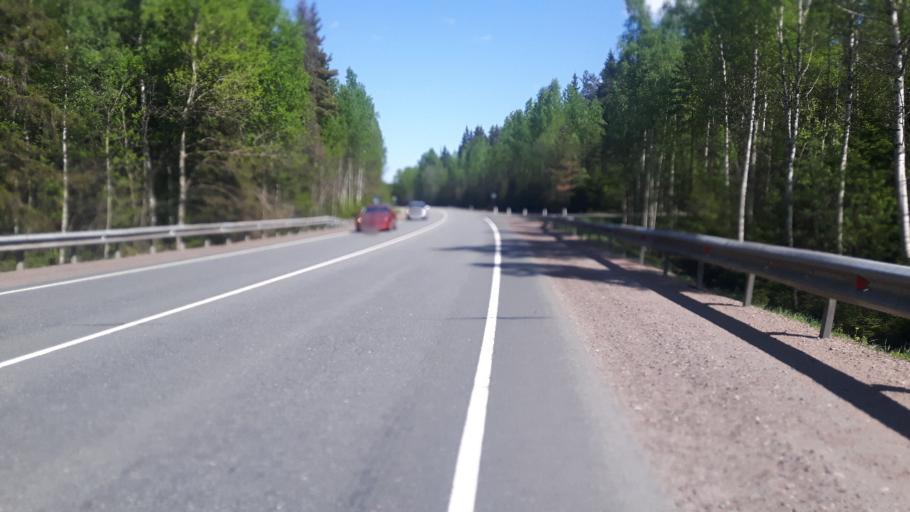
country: RU
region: Leningrad
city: Vysotsk
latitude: 60.6274
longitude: 28.2619
